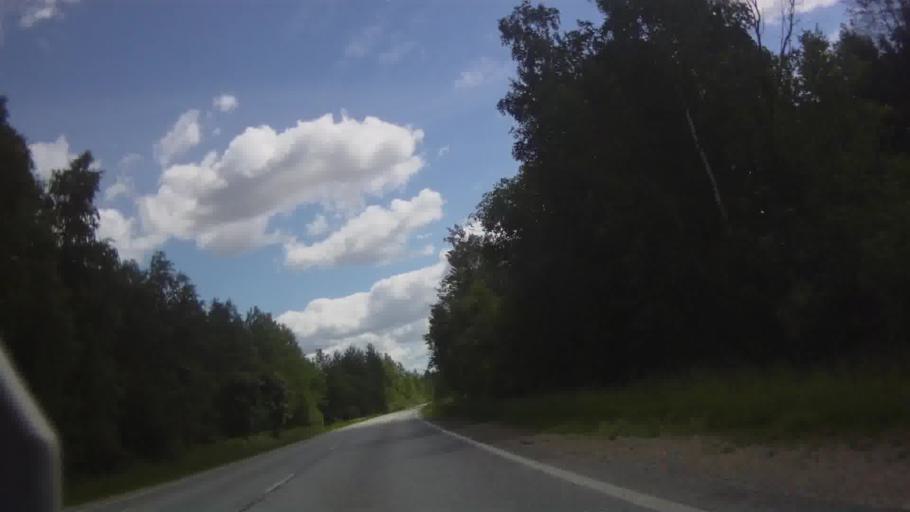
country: LV
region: Livani
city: Livani
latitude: 56.5289
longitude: 26.3917
